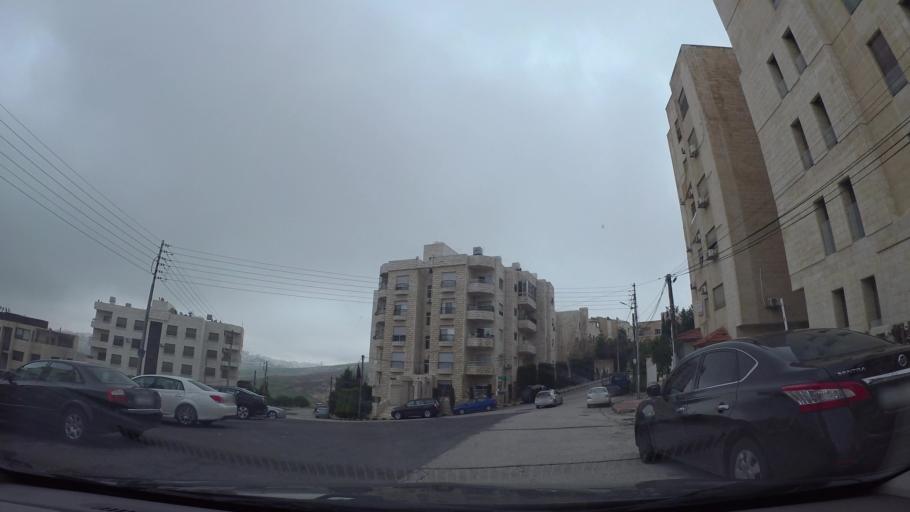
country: JO
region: Amman
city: Al Bunayyat ash Shamaliyah
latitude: 31.9362
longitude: 35.8704
